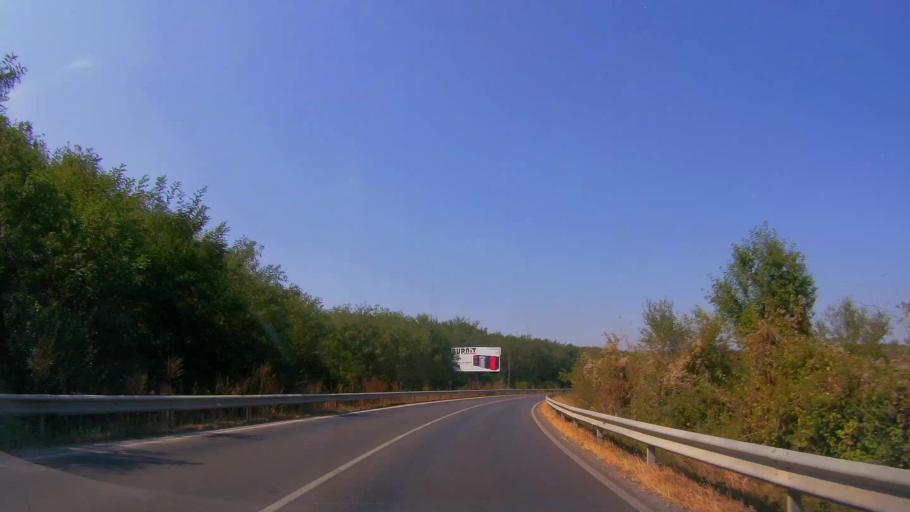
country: BG
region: Razgrad
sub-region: Obshtina Tsar Kaloyan
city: Tsar Kaloyan
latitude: 43.6152
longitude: 26.2155
